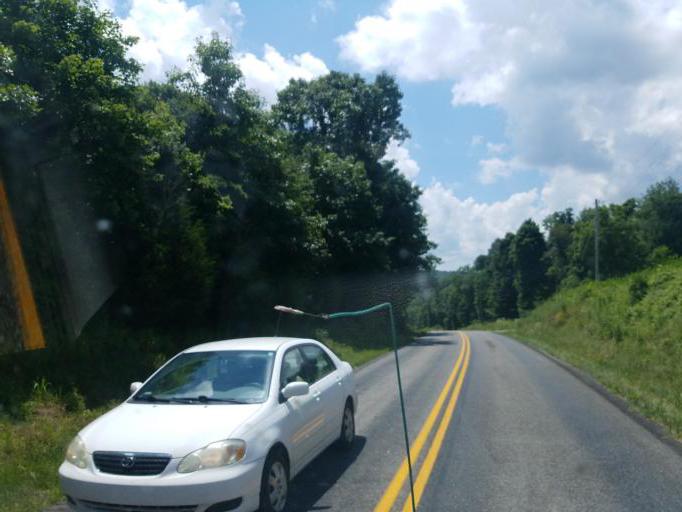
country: US
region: Kentucky
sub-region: Grayson County
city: Leitchfield
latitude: 37.5105
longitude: -86.4724
